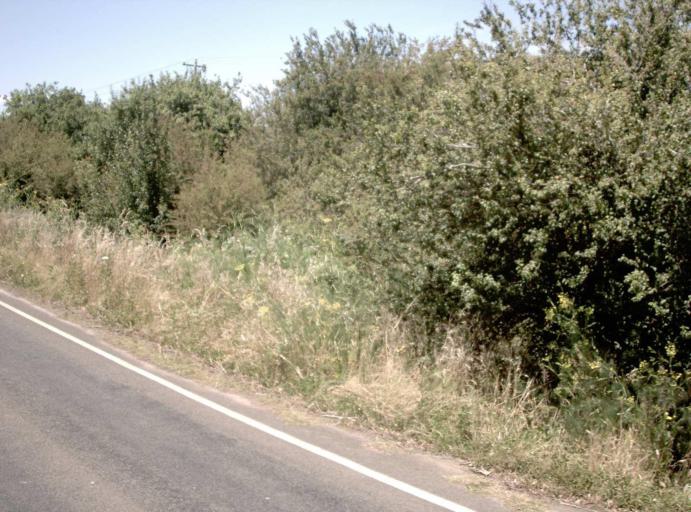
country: AU
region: Victoria
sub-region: Baw Baw
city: Warragul
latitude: -37.9722
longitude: 145.9509
